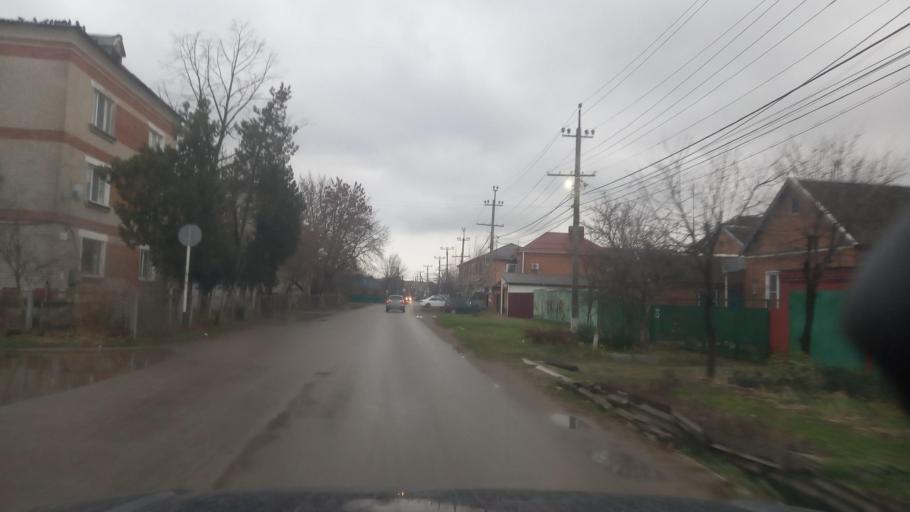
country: RU
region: Adygeya
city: Yablonovskiy
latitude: 44.9786
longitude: 38.9355
